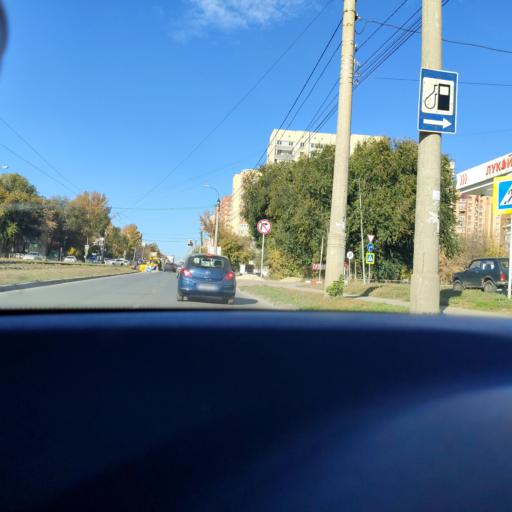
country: RU
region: Samara
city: Samara
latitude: 53.2307
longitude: 50.2264
